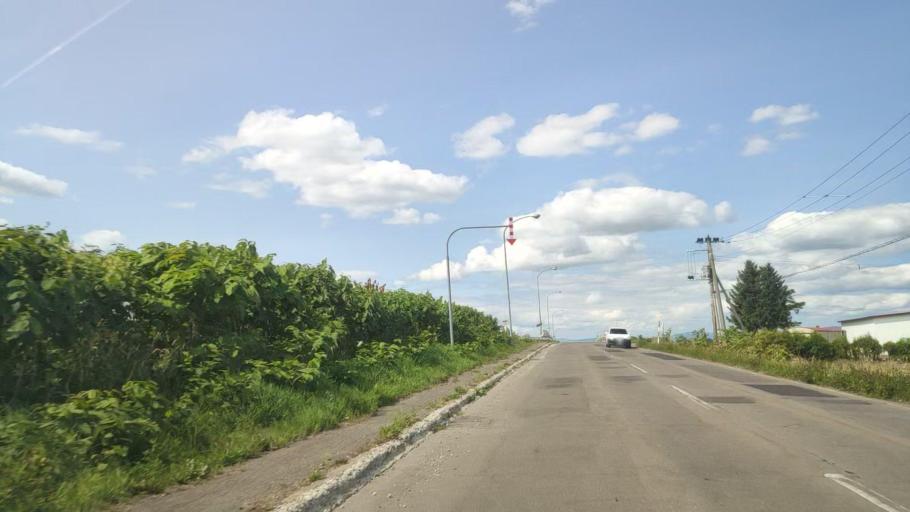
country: JP
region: Hokkaido
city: Nayoro
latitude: 44.2982
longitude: 142.4294
